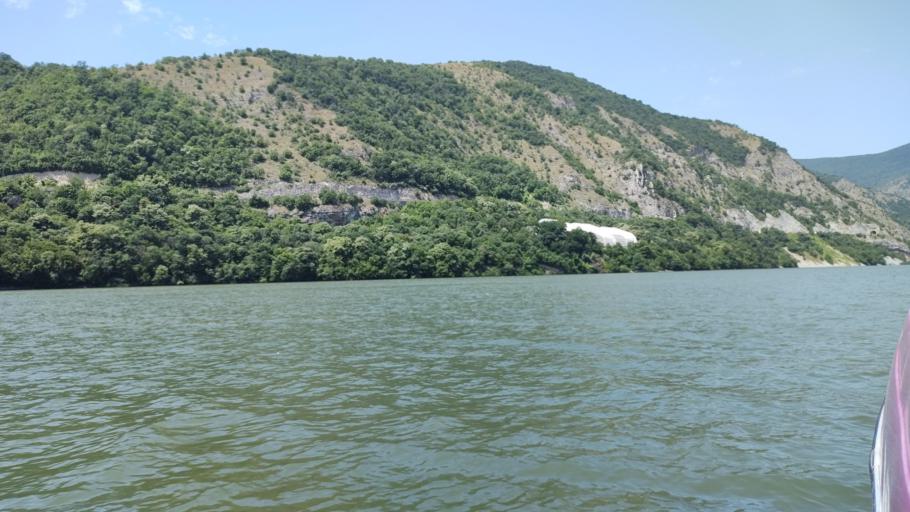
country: RO
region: Mehedinti
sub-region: Comuna Svinita
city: Svinita
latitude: 44.5540
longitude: 22.0318
